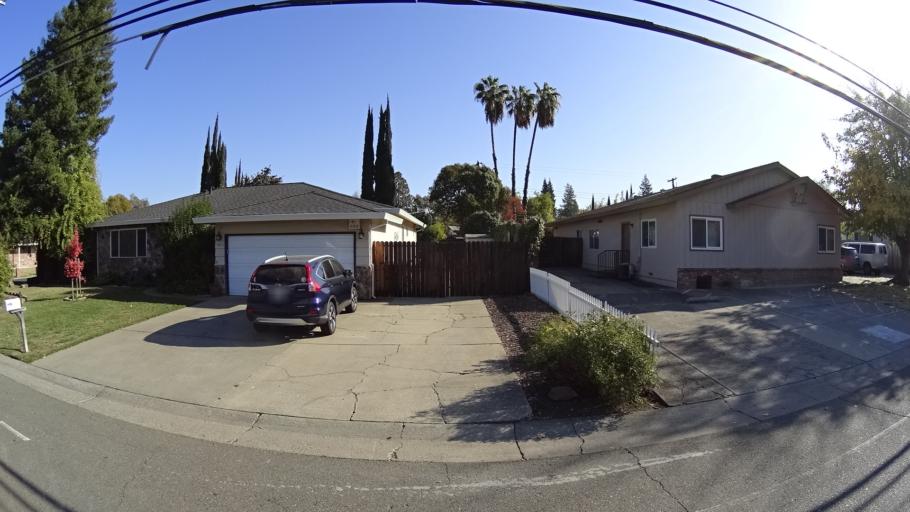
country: US
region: California
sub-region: Sacramento County
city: Fair Oaks
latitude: 38.6656
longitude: -121.2846
